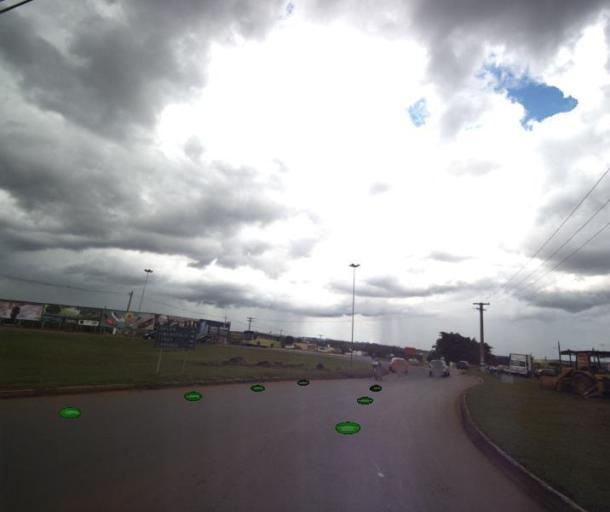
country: BR
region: Goias
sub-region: Anapolis
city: Anapolis
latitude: -16.2863
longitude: -48.9435
